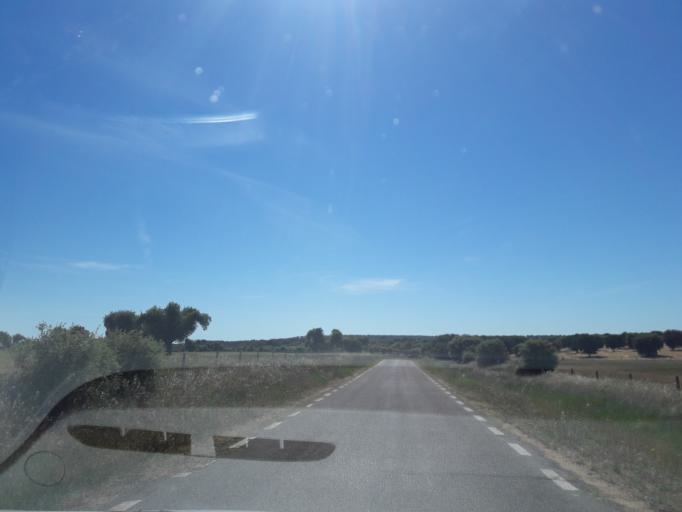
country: ES
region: Castille and Leon
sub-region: Provincia de Salamanca
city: Zarapicos
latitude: 41.0229
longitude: -5.8284
